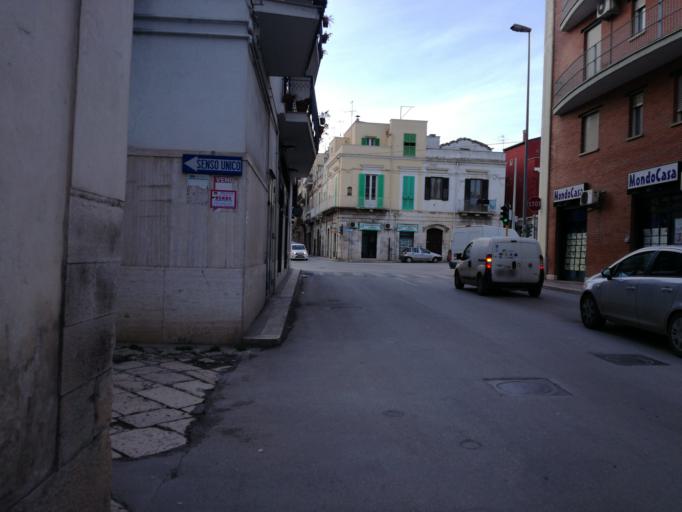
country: IT
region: Apulia
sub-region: Provincia di Bari
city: Corato
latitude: 41.1488
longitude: 16.4135
